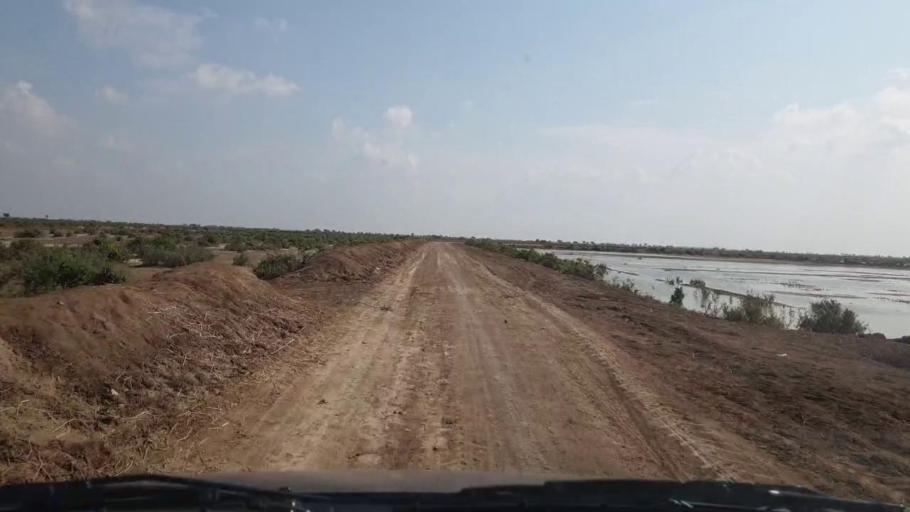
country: PK
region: Sindh
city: Badin
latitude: 24.4974
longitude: 68.6098
